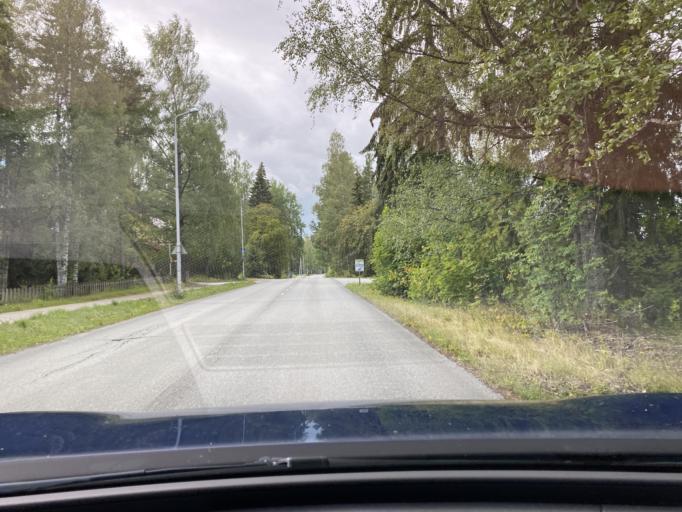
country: FI
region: Pirkanmaa
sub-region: Lounais-Pirkanmaa
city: Vammala
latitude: 61.3355
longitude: 22.9372
